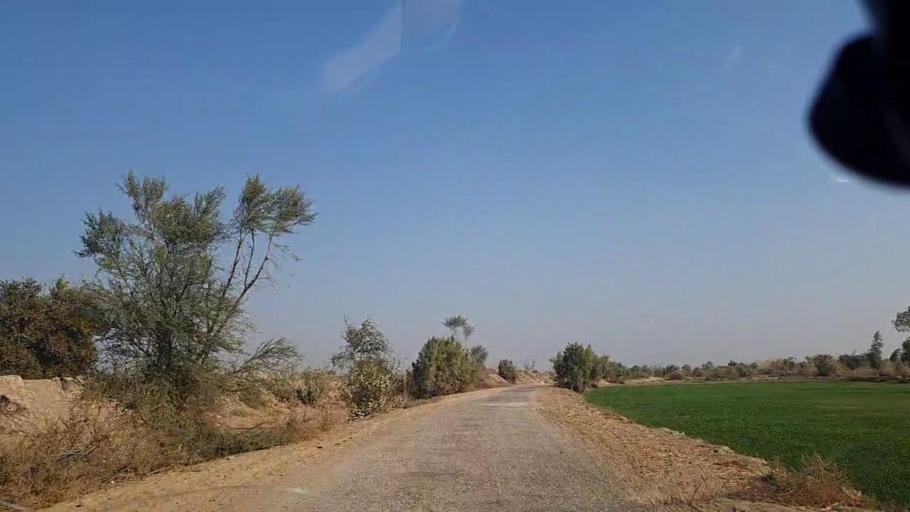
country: PK
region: Sindh
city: Khanpur
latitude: 27.6876
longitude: 69.5162
